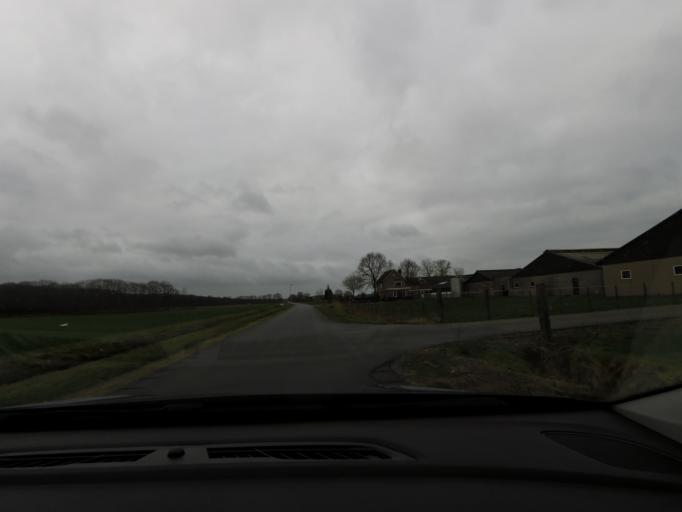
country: NL
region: North Brabant
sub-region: Gemeente Heusden
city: Heusden
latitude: 51.6734
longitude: 5.1722
